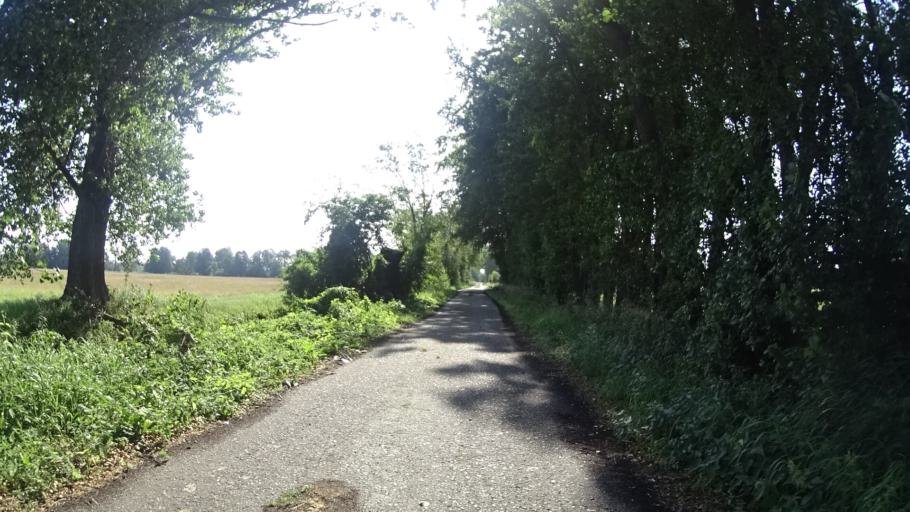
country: DE
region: Brandenburg
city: Neu Zauche
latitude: 51.9097
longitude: 14.0590
